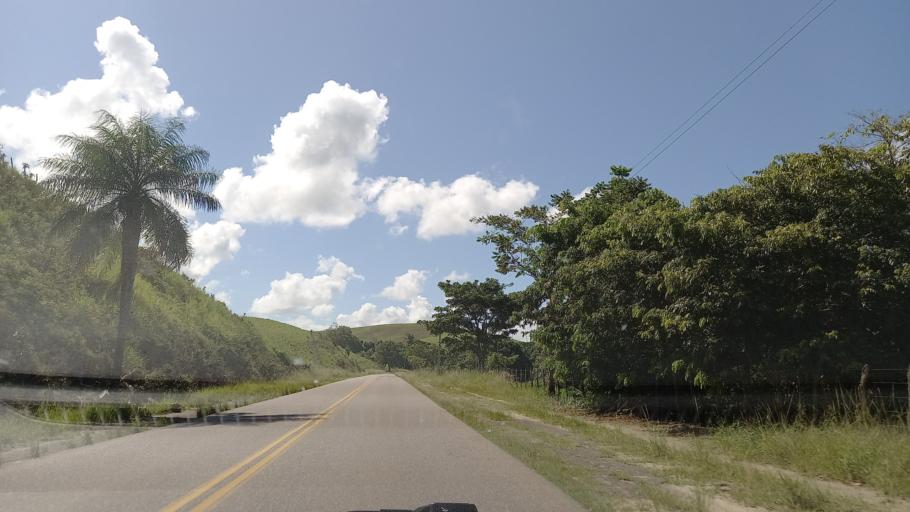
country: BR
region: Pernambuco
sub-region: Barreiros
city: Barreiros
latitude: -8.7545
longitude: -35.1710
